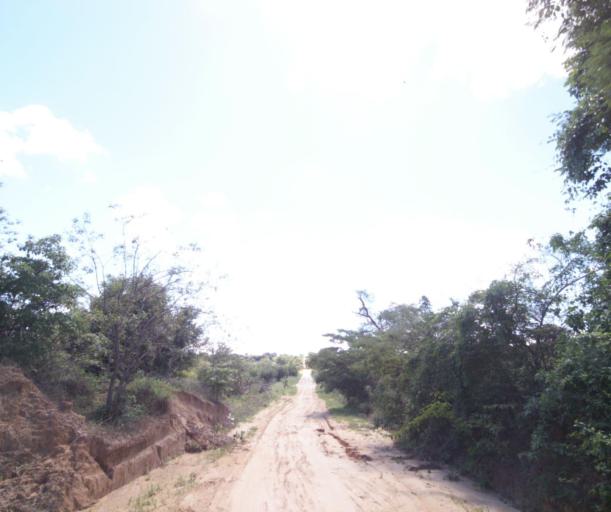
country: BR
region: Bahia
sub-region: Carinhanha
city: Carinhanha
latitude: -14.2354
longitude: -44.3166
